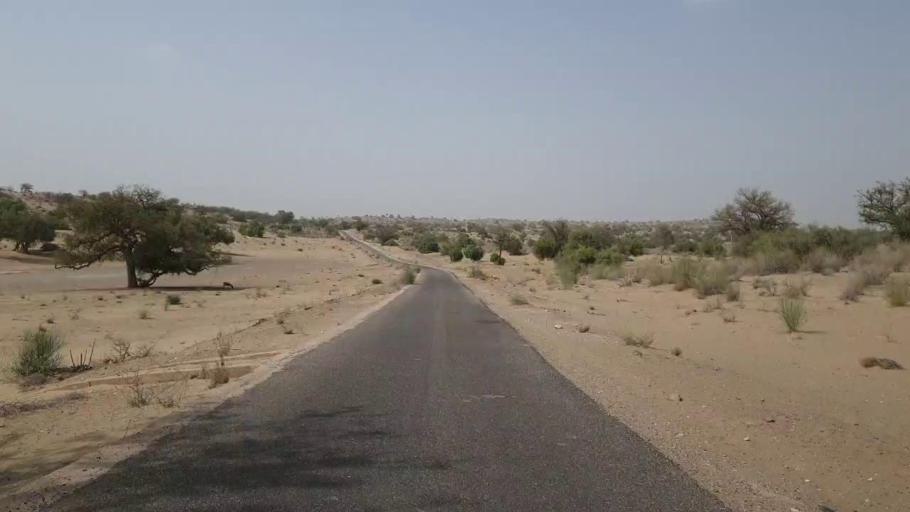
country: PK
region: Sindh
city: Mithi
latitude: 24.5896
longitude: 69.9231
